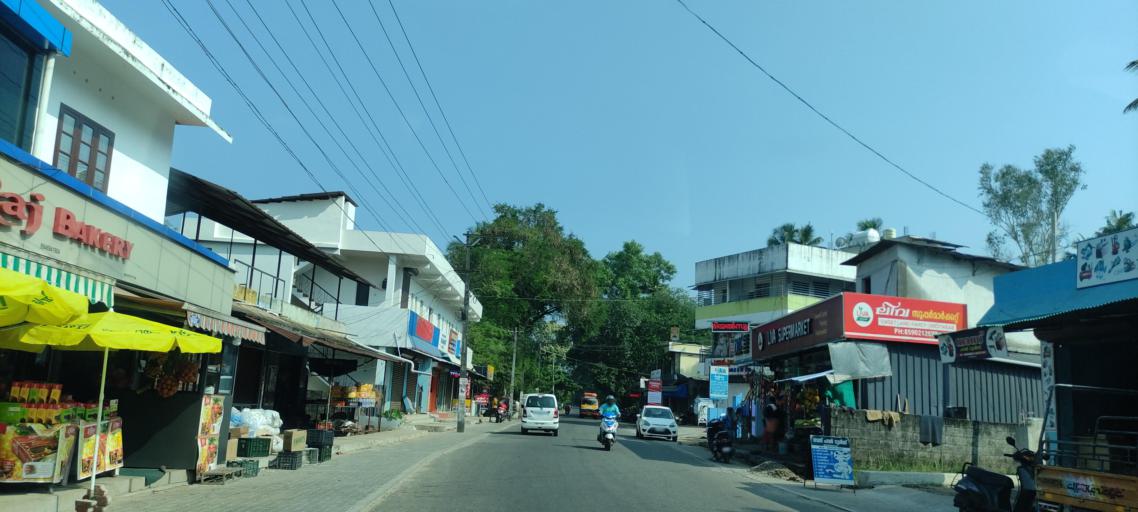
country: IN
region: Kerala
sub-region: Kollam
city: Panmana
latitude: 9.0525
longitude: 76.5610
